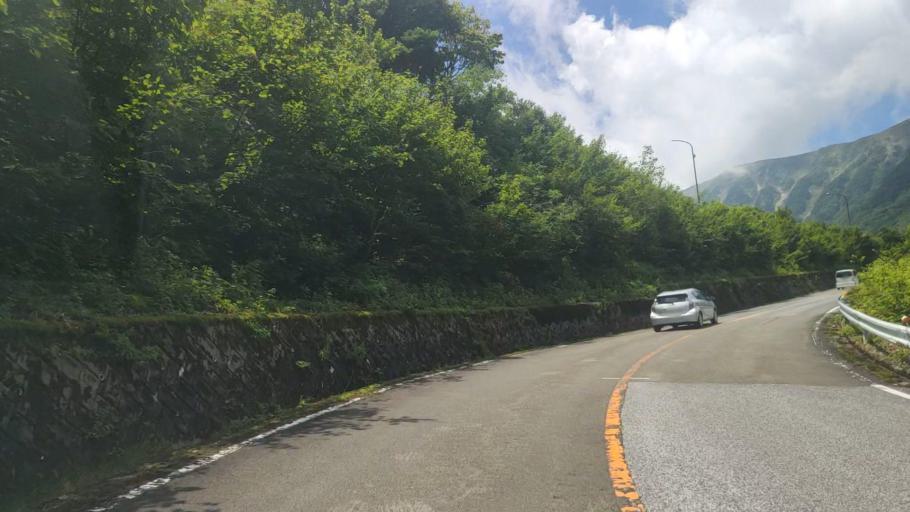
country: JP
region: Gifu
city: Tarui
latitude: 35.4083
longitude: 136.4235
